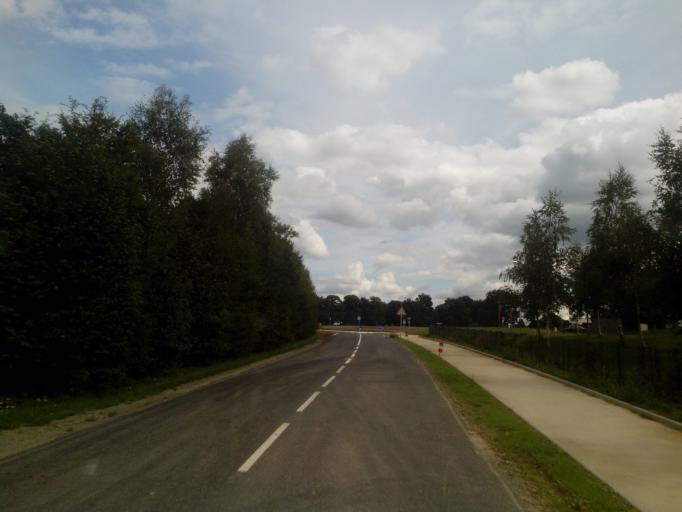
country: FR
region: Brittany
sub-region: Departement d'Ille-et-Vilaine
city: La Chapelle-des-Fougeretz
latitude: 48.1985
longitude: -1.7164
